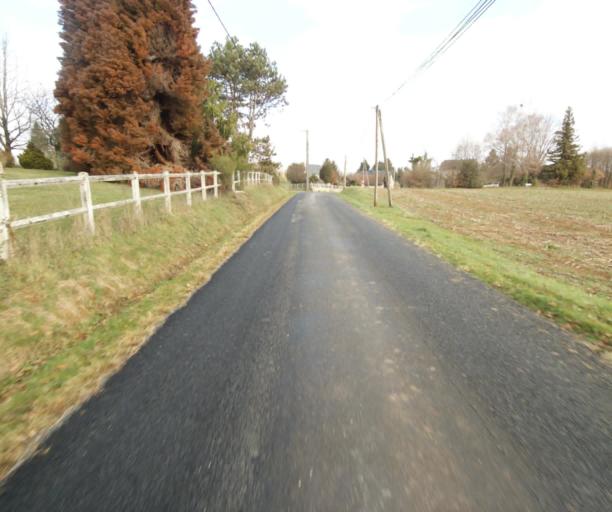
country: FR
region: Limousin
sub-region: Departement de la Correze
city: Saint-Mexant
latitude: 45.2781
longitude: 1.6076
